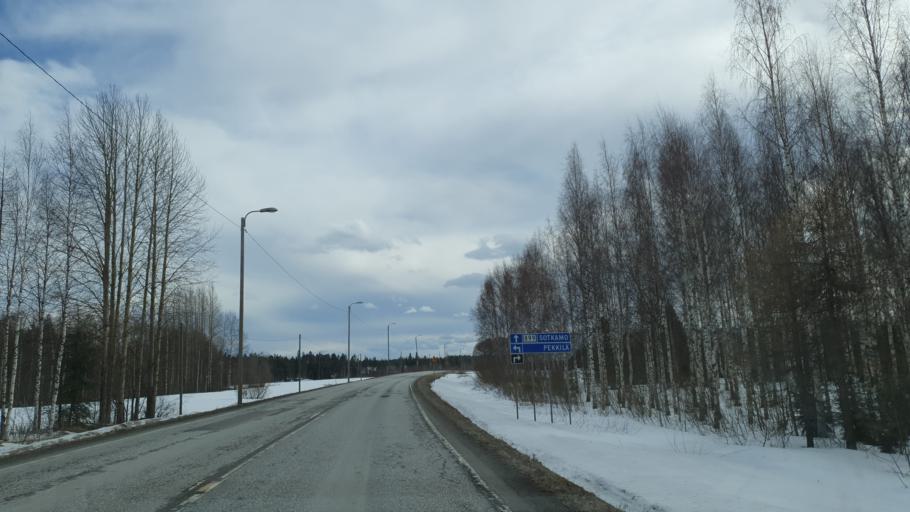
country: FI
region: Kainuu
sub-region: Kajaani
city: Vuokatti
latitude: 64.1651
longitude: 28.2487
